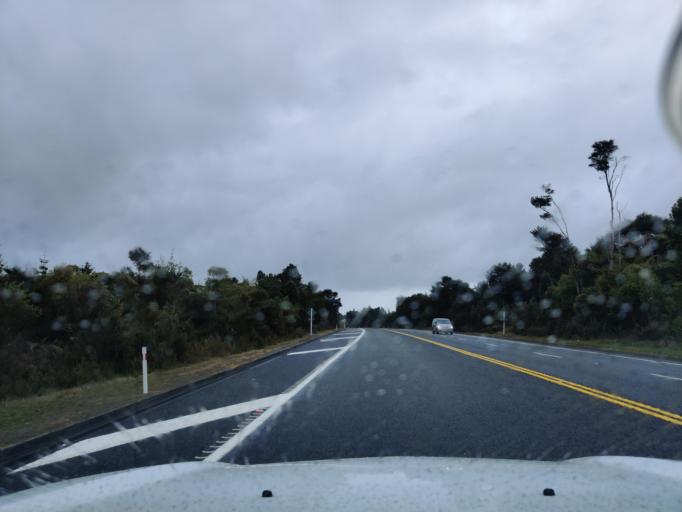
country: NZ
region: Waikato
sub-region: South Waikato District
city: Tokoroa
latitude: -38.0154
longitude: 175.9479
